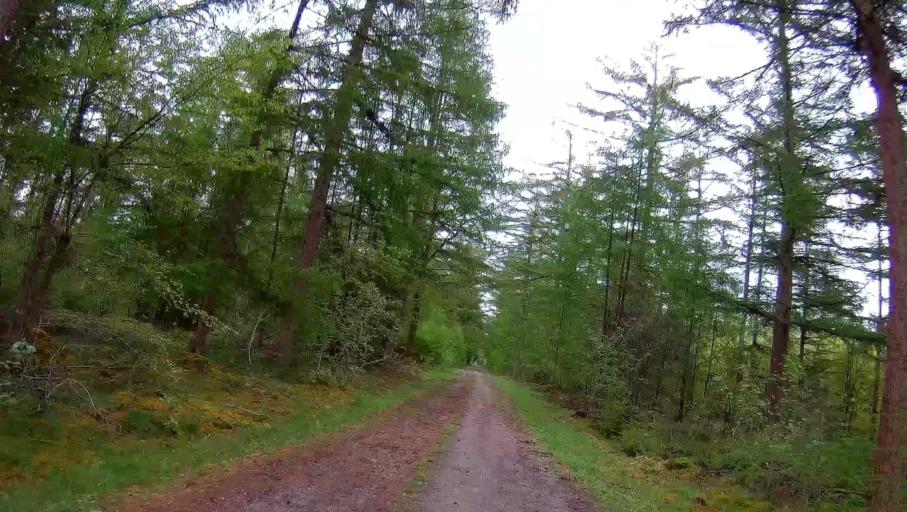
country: NL
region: Drenthe
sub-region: Gemeente Borger-Odoorn
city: Borger
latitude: 52.9444
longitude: 6.7571
